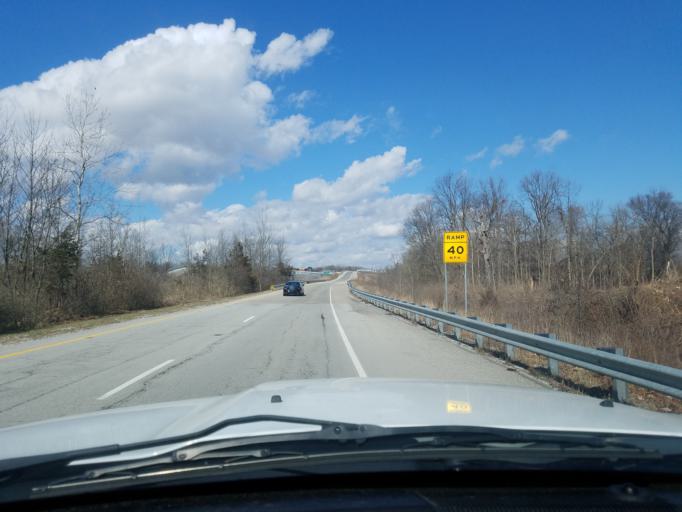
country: US
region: Indiana
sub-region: Hamilton County
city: Carmel
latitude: 39.9933
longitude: -86.1227
